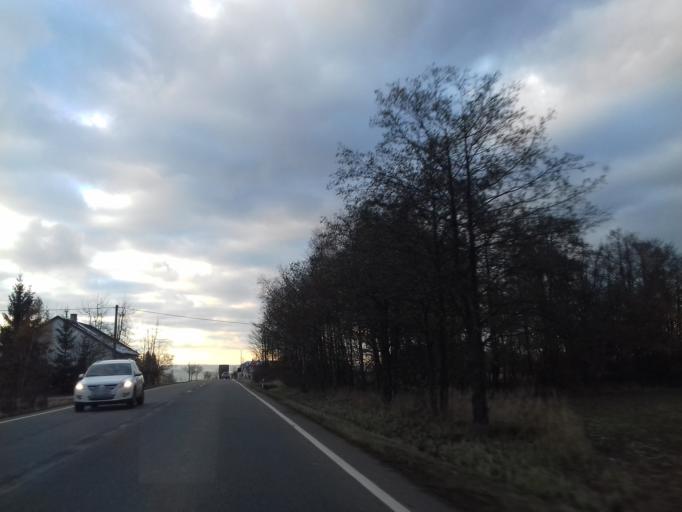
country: CZ
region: Pardubicky
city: Prosec
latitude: 49.7631
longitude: 16.1065
